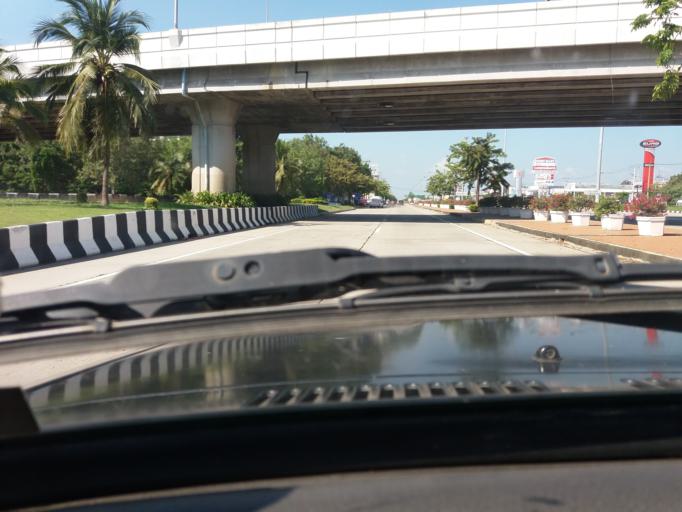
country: TH
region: Suphan Buri
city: Suphan Buri
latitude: 14.4650
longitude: 100.1311
